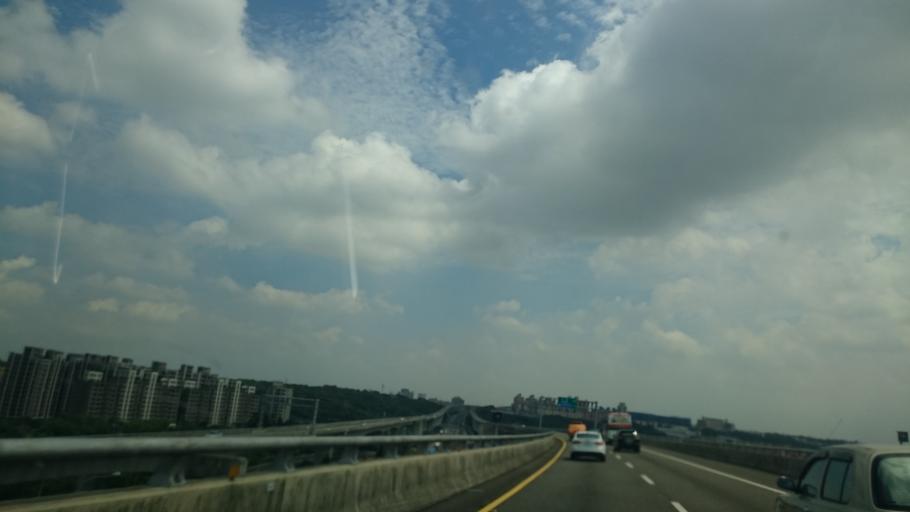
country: TW
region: Taiwan
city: Daxi
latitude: 24.9066
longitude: 121.1637
